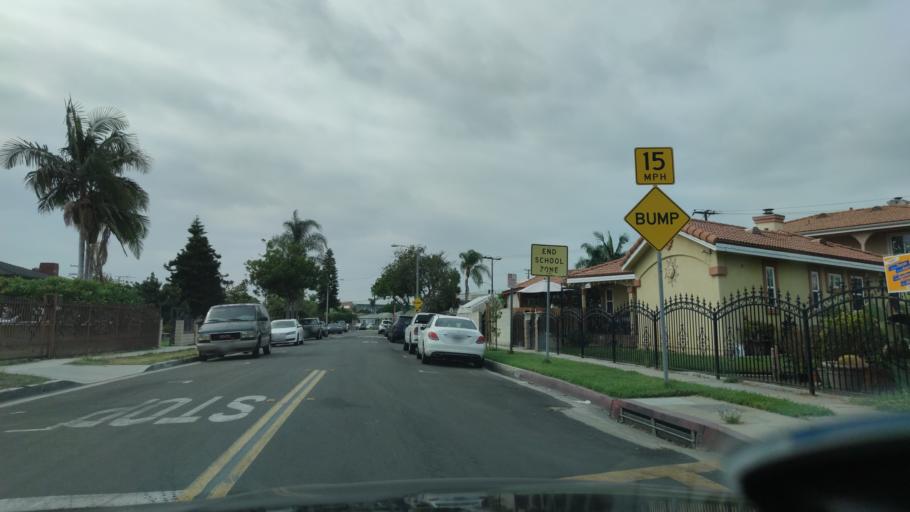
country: US
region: California
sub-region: Los Angeles County
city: Maywood
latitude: 33.9932
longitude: -118.1847
